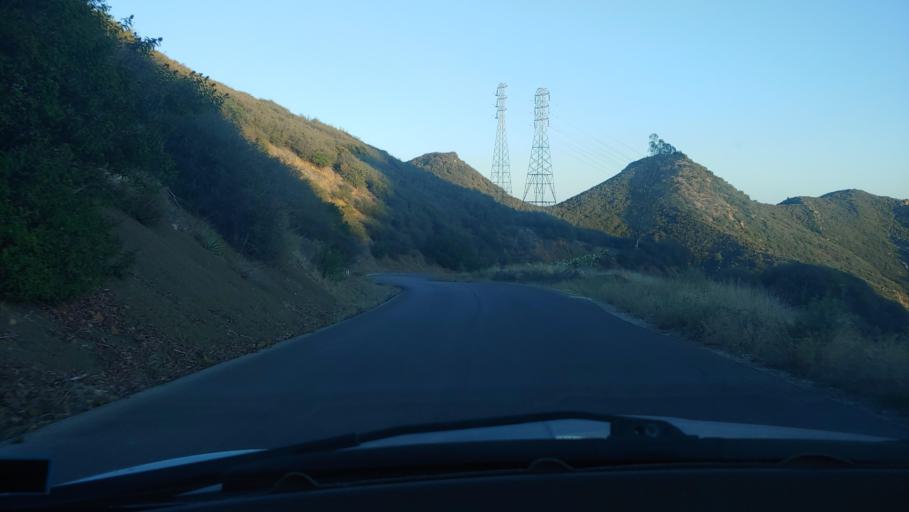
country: US
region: California
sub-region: Santa Barbara County
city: Mission Canyon
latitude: 34.4684
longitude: -119.6733
